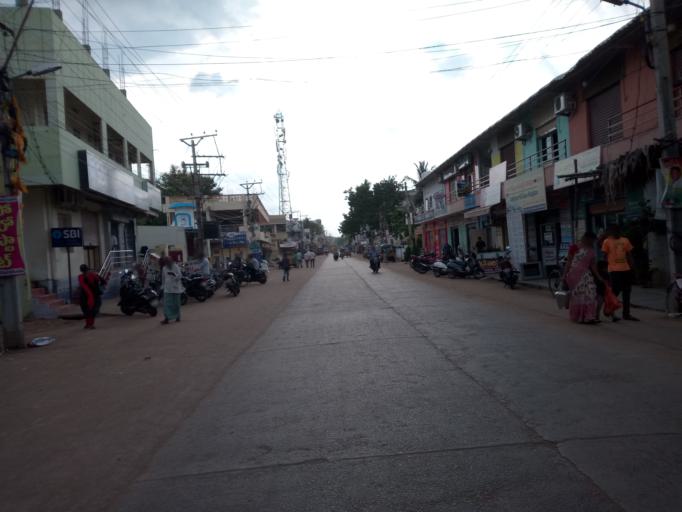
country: IN
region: Andhra Pradesh
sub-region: Guntur
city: Tadepalle
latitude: 16.4914
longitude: 80.6007
